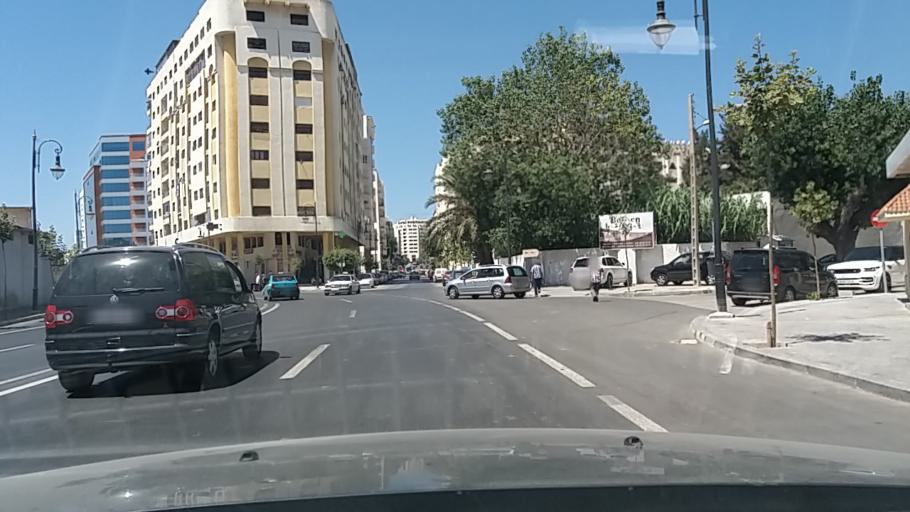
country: MA
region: Tanger-Tetouan
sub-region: Tanger-Assilah
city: Tangier
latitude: 35.7719
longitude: -5.7983
